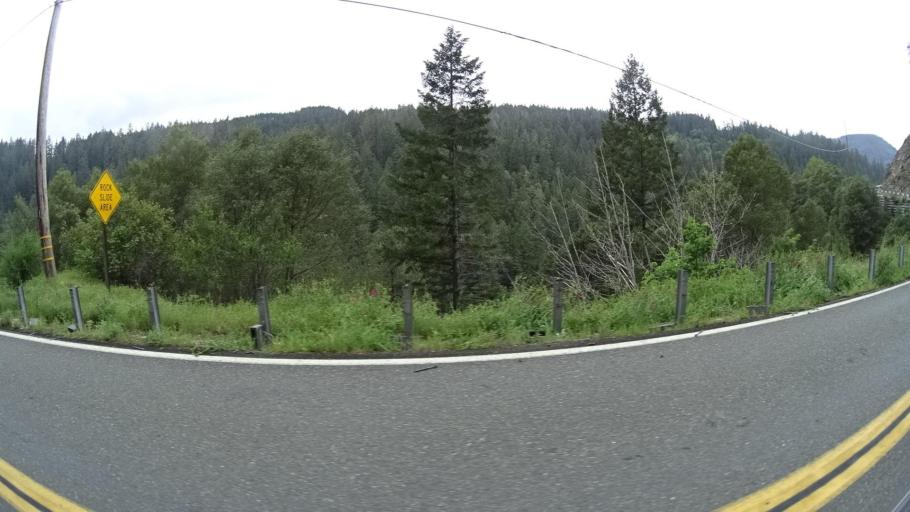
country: US
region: California
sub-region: Humboldt County
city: Willow Creek
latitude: 41.1185
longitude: -123.6882
